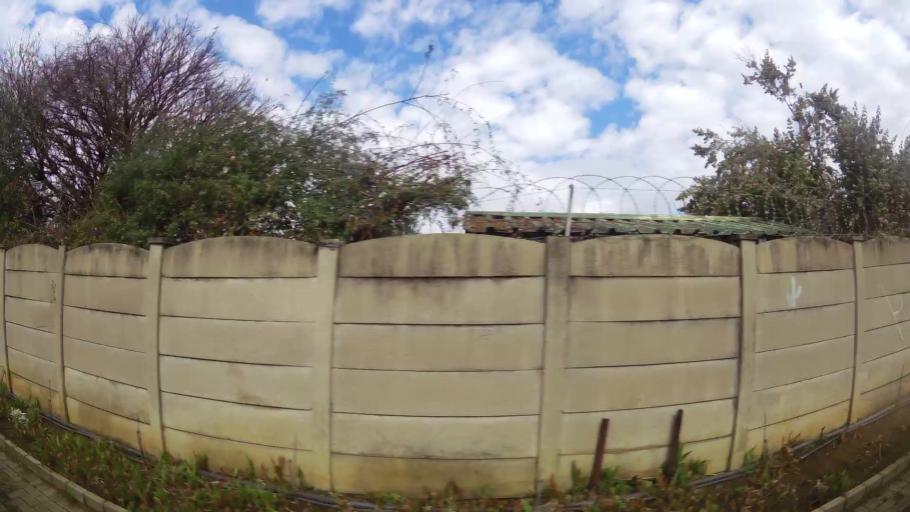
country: ZA
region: Gauteng
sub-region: Sedibeng District Municipality
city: Vereeniging
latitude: -26.6517
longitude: 27.9763
